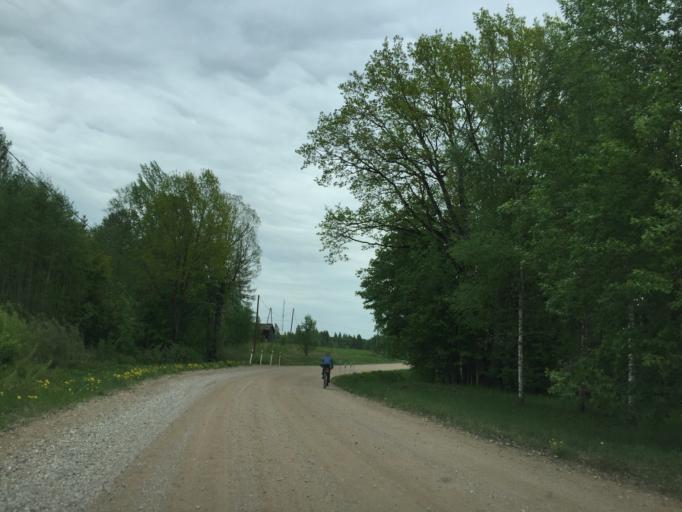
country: LV
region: Lielvarde
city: Lielvarde
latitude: 56.8045
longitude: 24.8613
